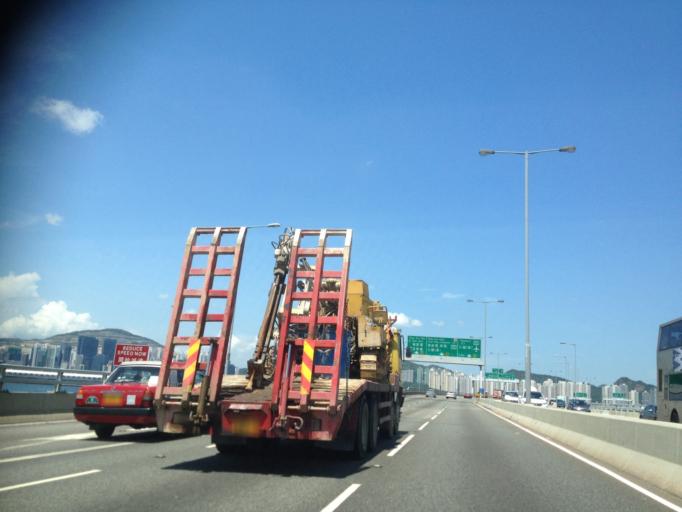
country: HK
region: Kowloon City
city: Kowloon
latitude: 22.2939
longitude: 114.2016
